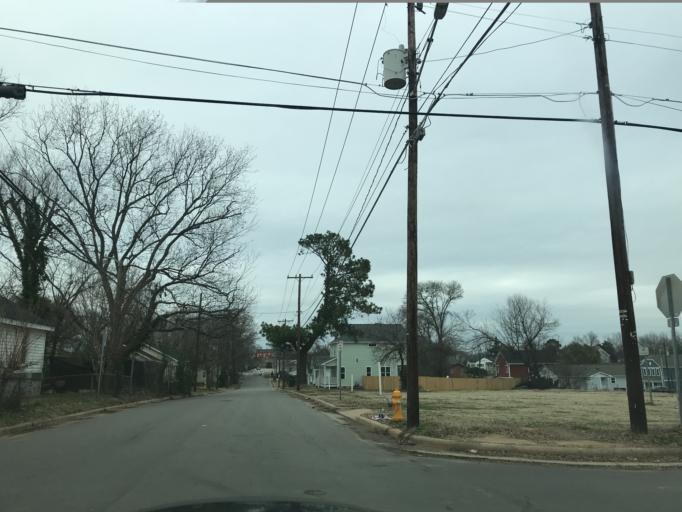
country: US
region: North Carolina
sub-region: Wake County
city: Raleigh
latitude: 35.7824
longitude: -78.6175
